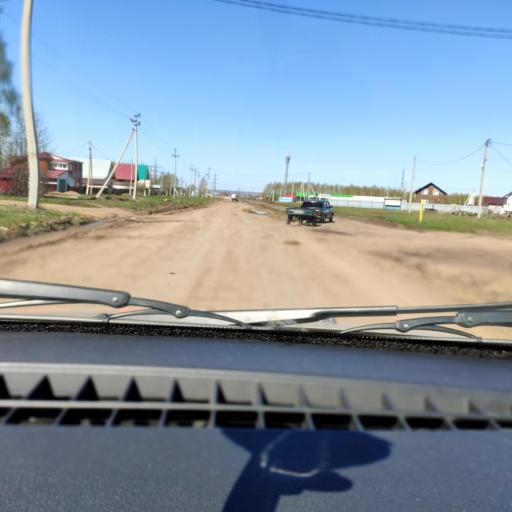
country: RU
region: Bashkortostan
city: Iglino
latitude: 54.8193
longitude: 56.4250
